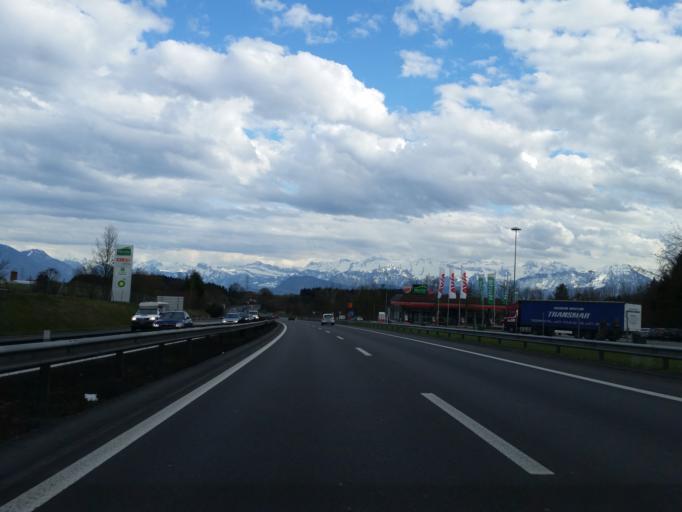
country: CH
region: Lucerne
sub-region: Sursee District
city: Neuenkirch
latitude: 47.1122
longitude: 8.2321
